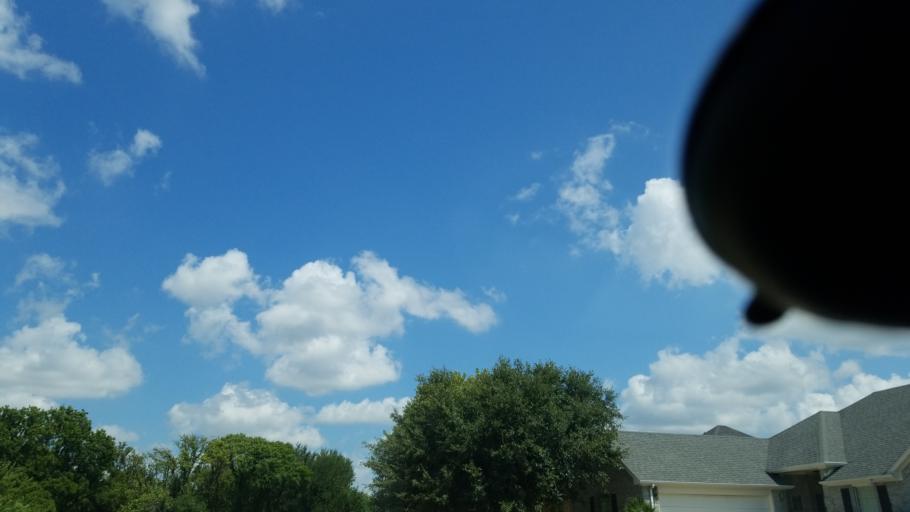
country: US
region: Texas
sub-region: Dallas County
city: Grand Prairie
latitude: 32.7245
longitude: -96.9902
